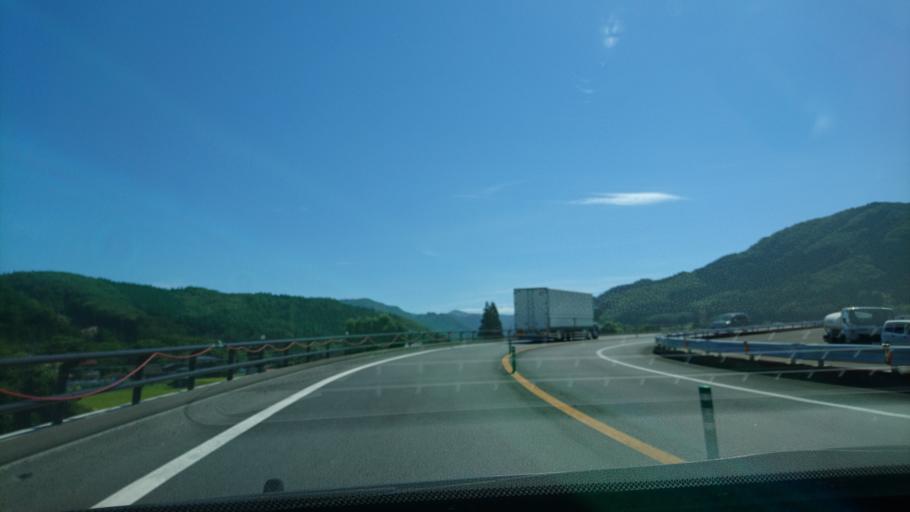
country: JP
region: Iwate
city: Tono
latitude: 39.2659
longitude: 141.5889
